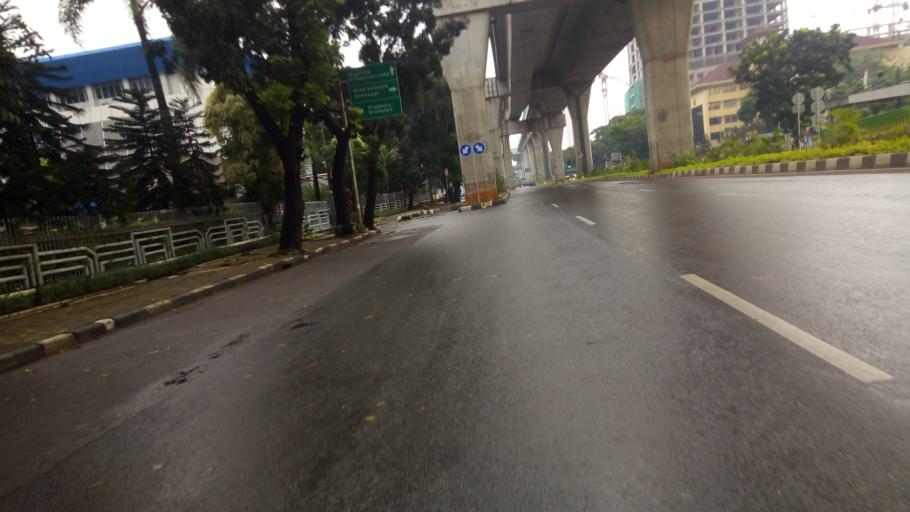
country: ID
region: Jakarta Raya
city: Jakarta
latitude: -6.2400
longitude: 106.8036
